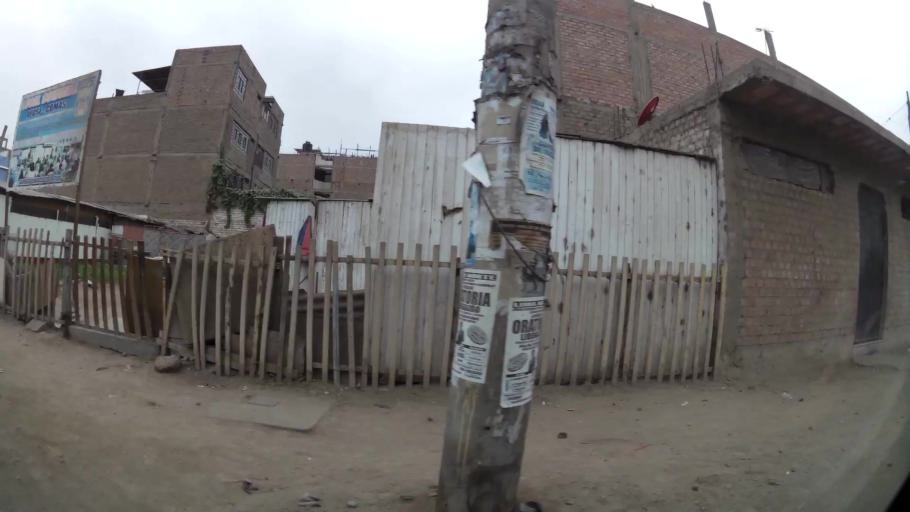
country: PE
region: Lima
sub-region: Lima
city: Independencia
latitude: -11.9616
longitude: -77.0613
